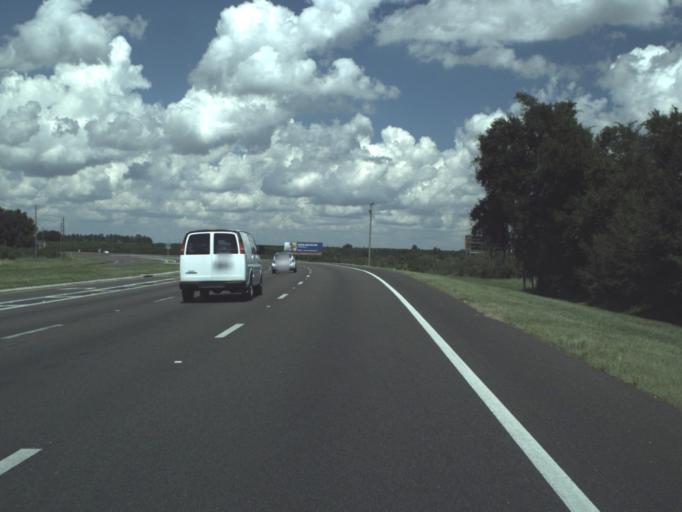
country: US
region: Florida
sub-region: Polk County
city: Lake Hamilton
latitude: 28.0467
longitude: -81.6343
